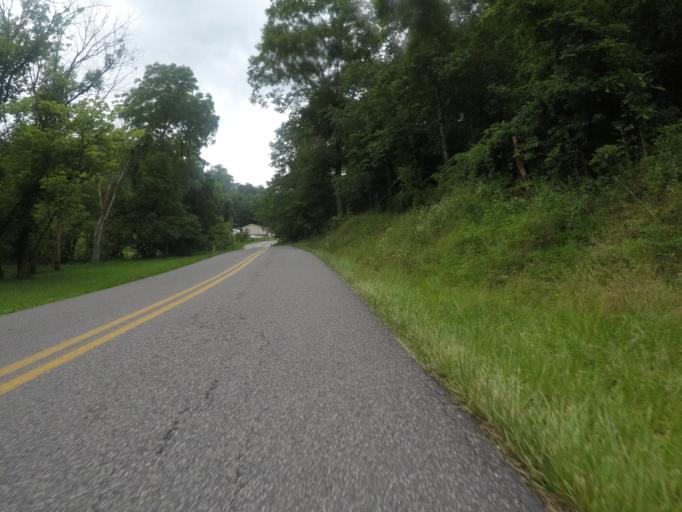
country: US
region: West Virginia
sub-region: Wayne County
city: Lavalette
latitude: 38.3634
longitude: -82.4264
